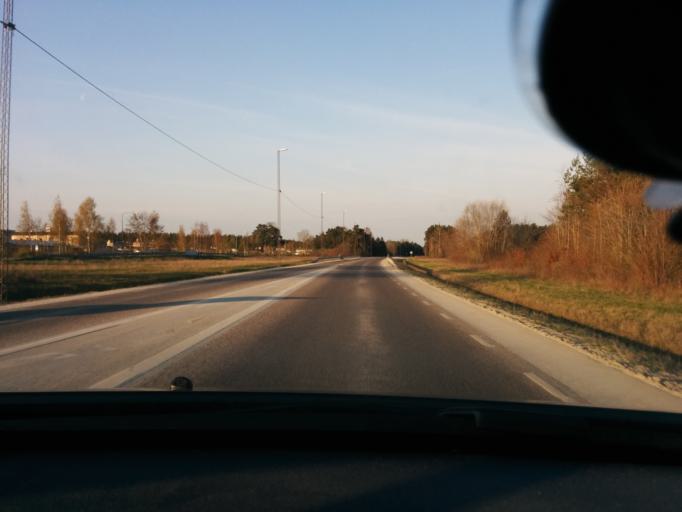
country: SE
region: Gotland
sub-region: Gotland
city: Visby
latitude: 57.6150
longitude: 18.3118
